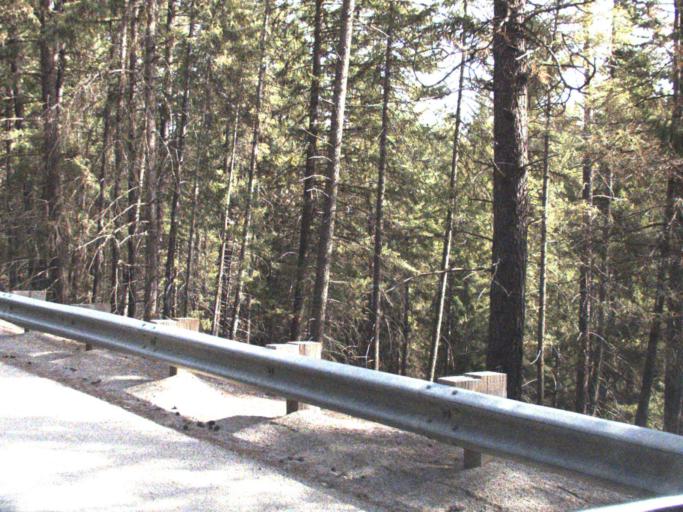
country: US
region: Washington
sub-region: Stevens County
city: Colville
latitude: 48.5056
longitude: -117.7076
